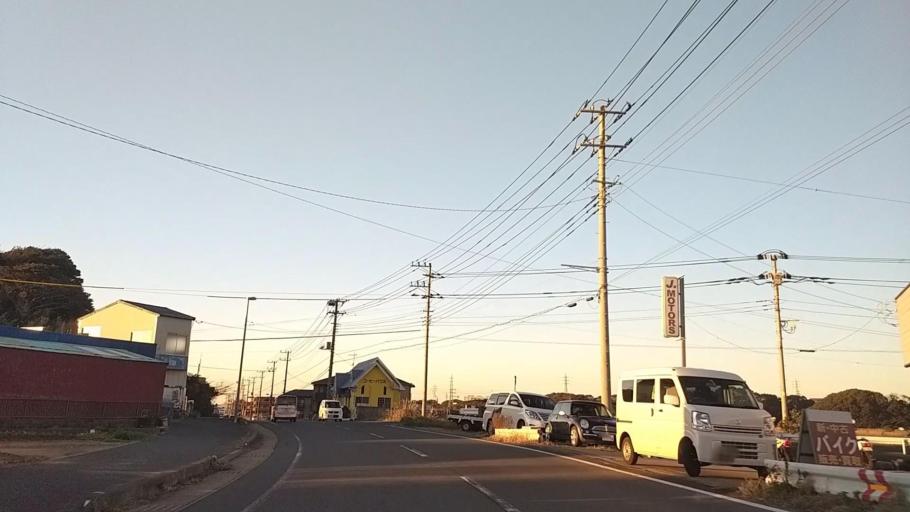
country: JP
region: Chiba
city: Hasaki
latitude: 35.7141
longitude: 140.8408
